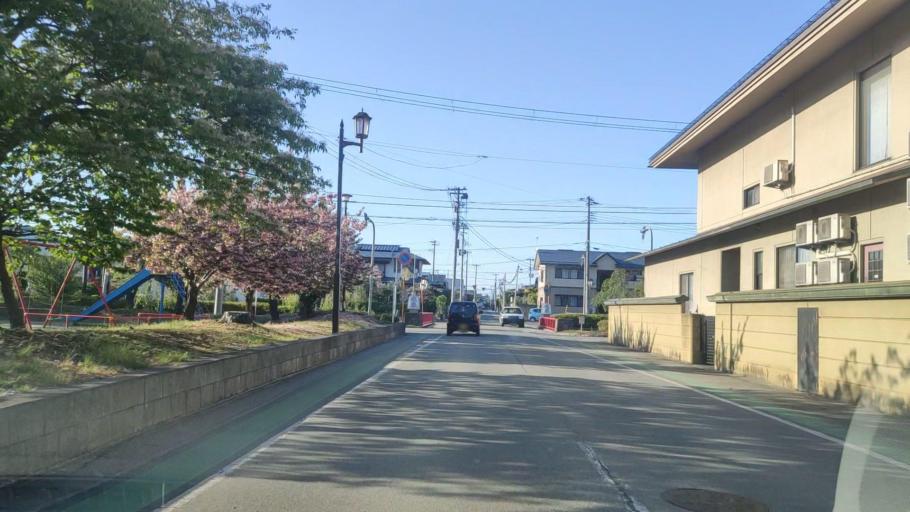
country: JP
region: Yamagata
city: Tendo
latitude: 38.3609
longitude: 140.3843
